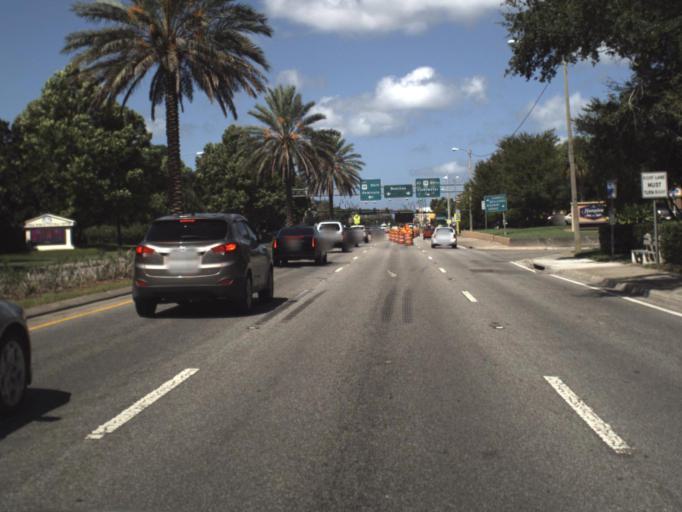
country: US
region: Florida
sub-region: Pinellas County
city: Largo
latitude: 27.9168
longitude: -82.7850
